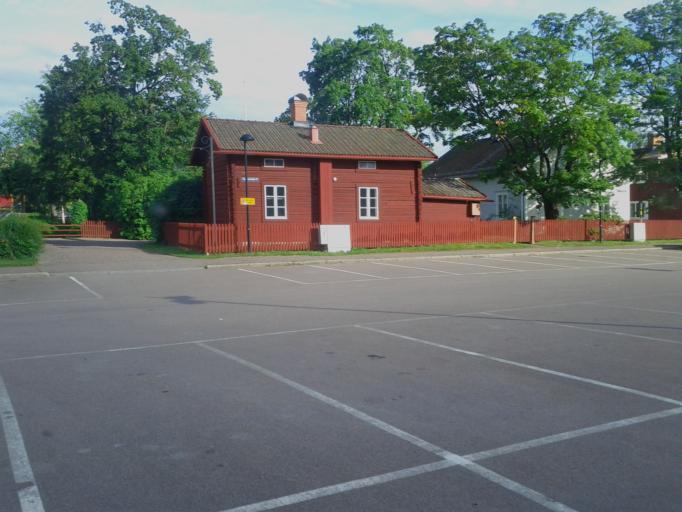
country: SE
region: Dalarna
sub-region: Borlange Kommun
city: Borlaenge
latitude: 60.4845
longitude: 15.4284
